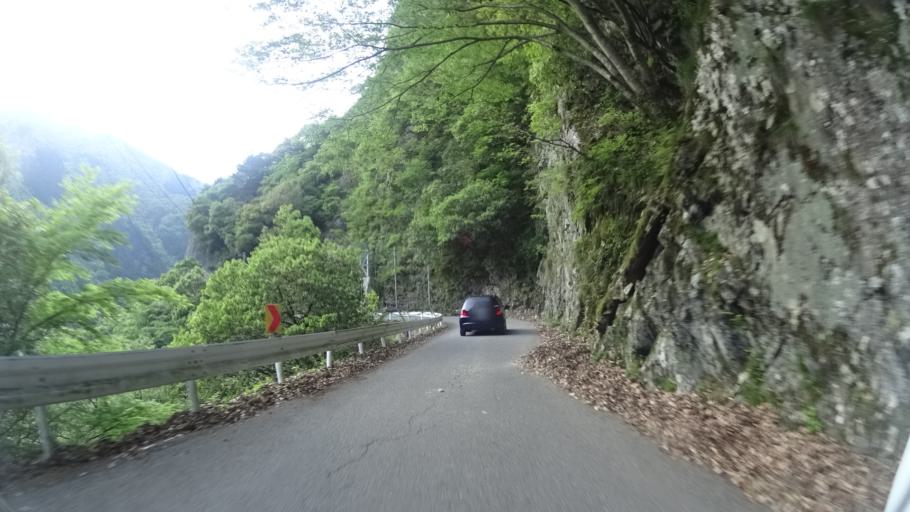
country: JP
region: Tokushima
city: Ikedacho
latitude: 33.9032
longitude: 133.8137
